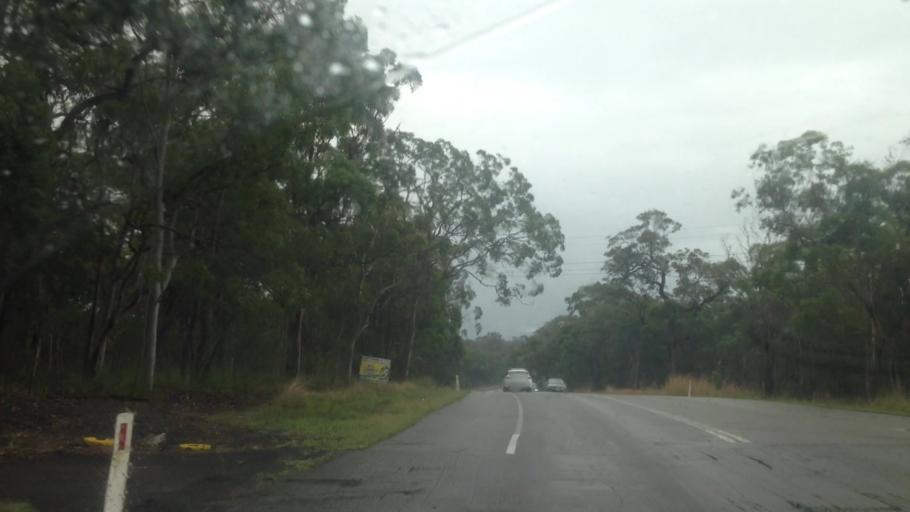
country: AU
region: New South Wales
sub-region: Lake Macquarie Shire
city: Dora Creek
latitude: -33.1294
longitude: 151.4764
